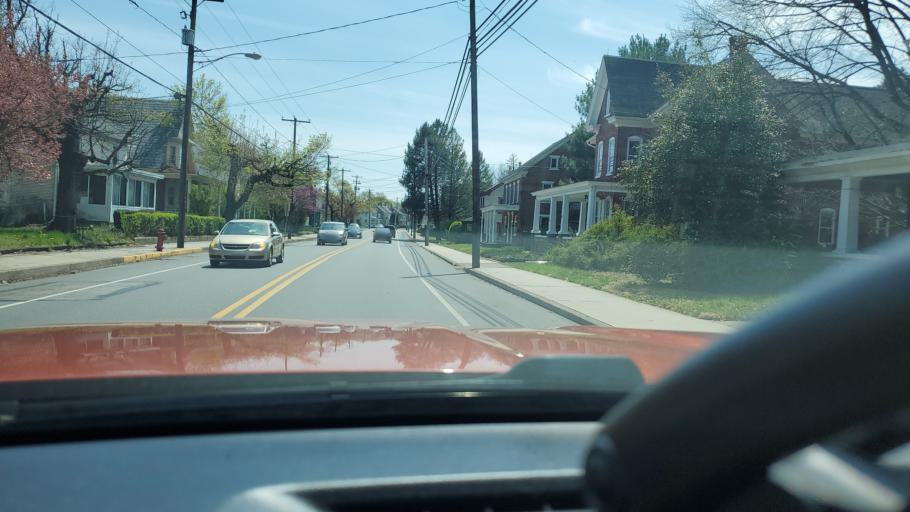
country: US
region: Pennsylvania
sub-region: Montgomery County
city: Red Hill
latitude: 40.3734
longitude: -75.4819
